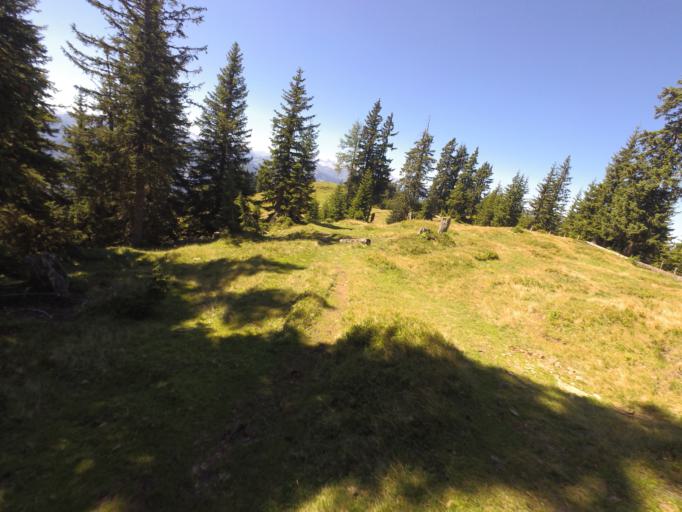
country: AT
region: Salzburg
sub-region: Politischer Bezirk Sankt Johann im Pongau
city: Goldegg
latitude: 47.3508
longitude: 13.0703
